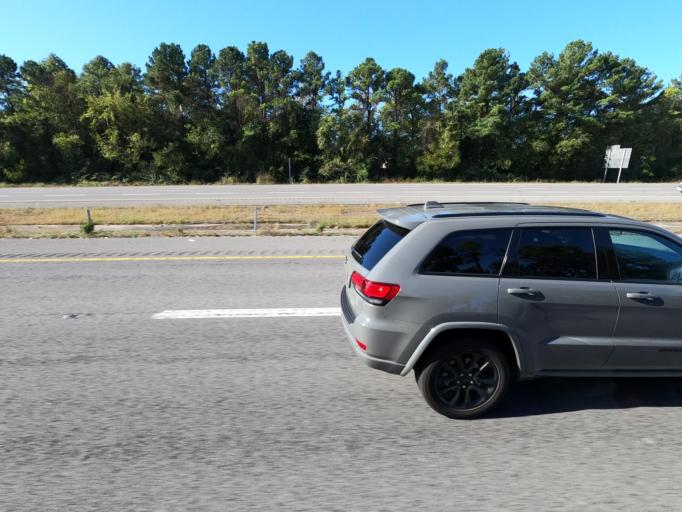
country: US
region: Tennessee
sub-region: Rutherford County
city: Murfreesboro
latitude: 35.8749
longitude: -86.4654
